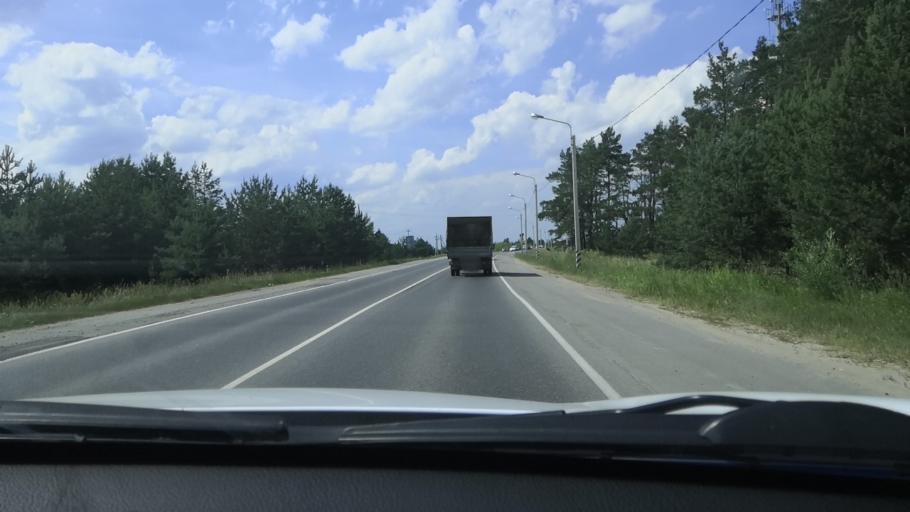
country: RU
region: Rjazan
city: Murmino
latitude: 54.6307
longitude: 39.9531
